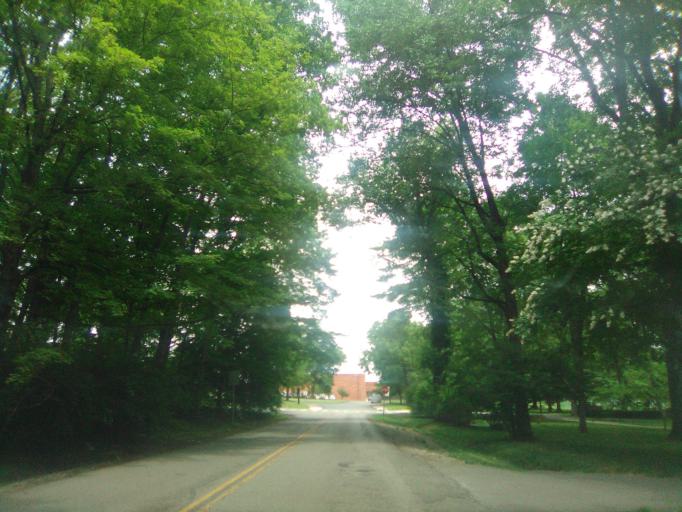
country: US
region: Tennessee
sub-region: Davidson County
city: Belle Meade
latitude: 36.1164
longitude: -86.8734
